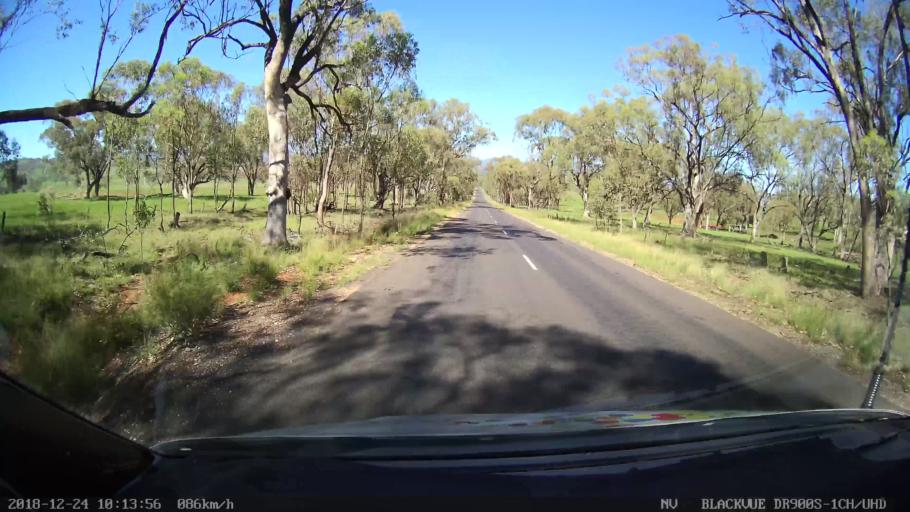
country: AU
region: New South Wales
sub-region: Liverpool Plains
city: Quirindi
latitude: -31.6939
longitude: 150.6352
